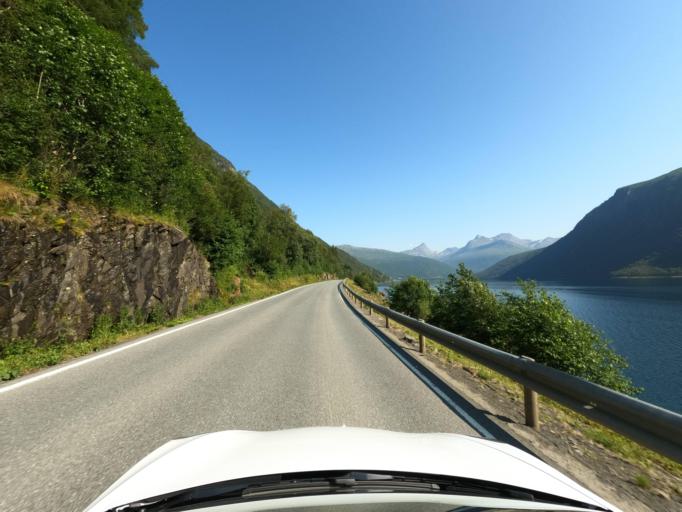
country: NO
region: Nordland
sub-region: Narvik
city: Narvik
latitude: 68.3966
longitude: 17.5137
